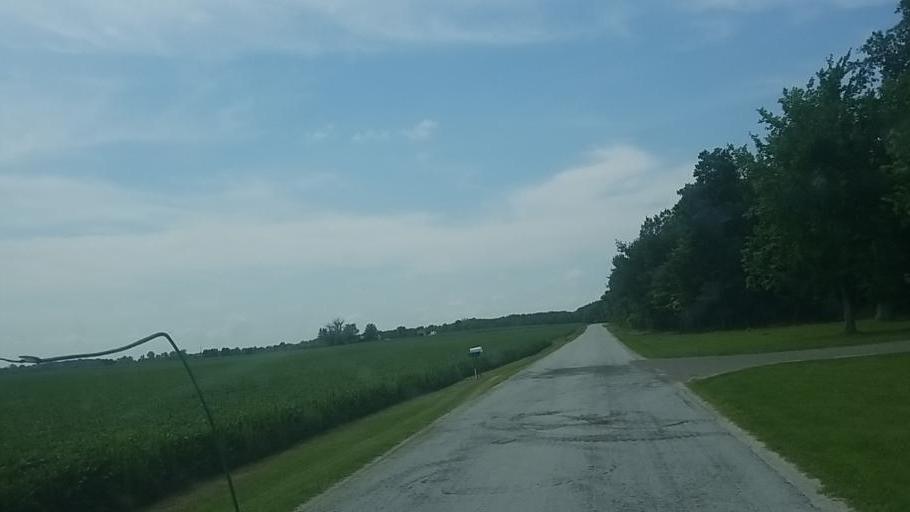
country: US
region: Ohio
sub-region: Hardin County
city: Forest
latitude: 40.6513
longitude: -83.4341
